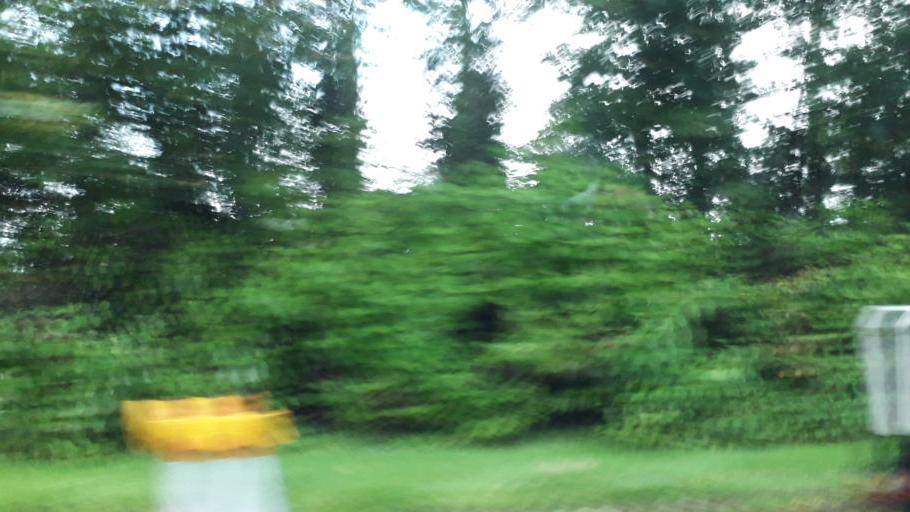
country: IE
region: Leinster
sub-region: An Longfort
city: Longford
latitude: 53.7220
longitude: -7.7611
